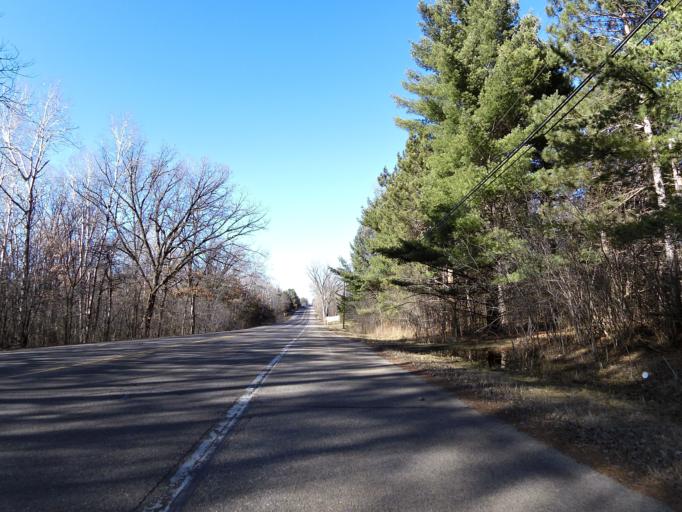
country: US
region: Minnesota
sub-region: Washington County
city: Lakeland
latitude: 44.9693
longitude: -92.8223
